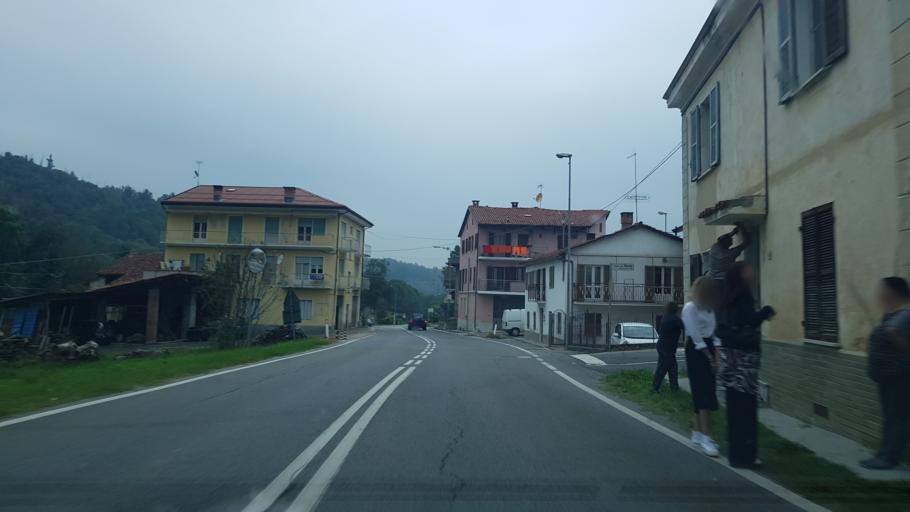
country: IT
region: Piedmont
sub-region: Provincia di Cuneo
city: Frabosa Sottana
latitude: 44.3270
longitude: 7.7946
